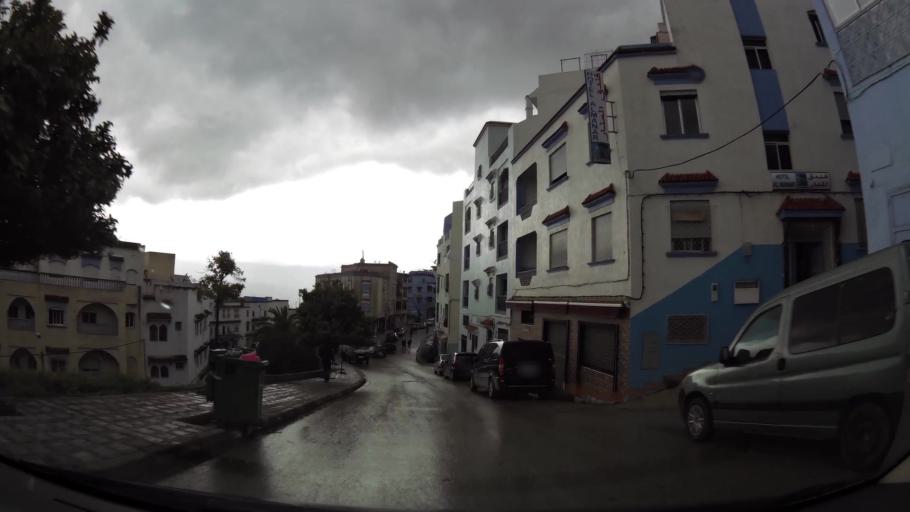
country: MA
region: Tanger-Tetouan
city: Chefchaouene
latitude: 35.1702
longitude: -5.2679
